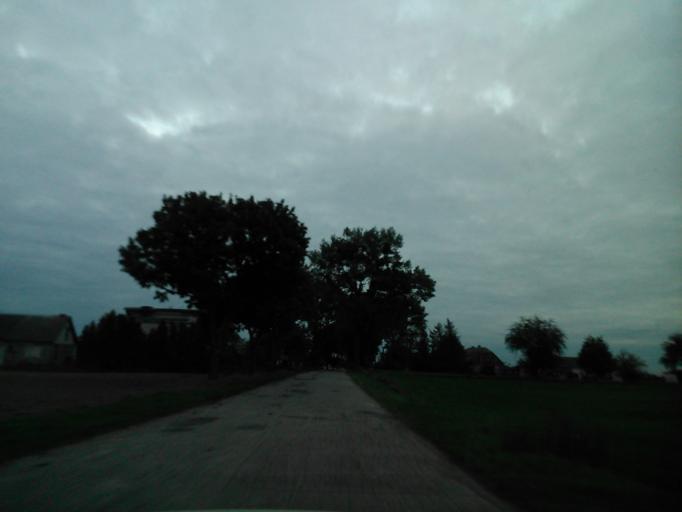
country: PL
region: Kujawsko-Pomorskie
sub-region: Powiat golubsko-dobrzynski
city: Kowalewo Pomorskie
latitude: 53.1081
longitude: 18.8731
